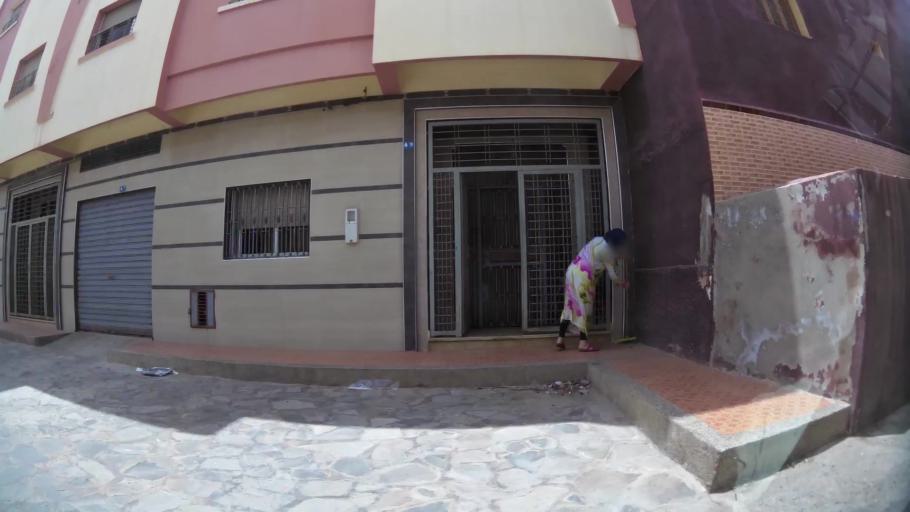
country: MA
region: Oriental
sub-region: Nador
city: Nador
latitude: 35.1685
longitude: -2.9174
